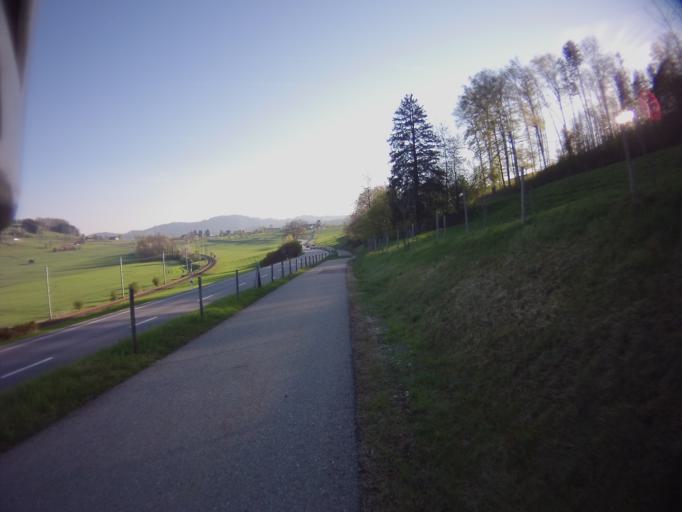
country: CH
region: Zurich
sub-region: Bezirk Affoltern
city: Hedingen
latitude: 47.3089
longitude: 8.4539
